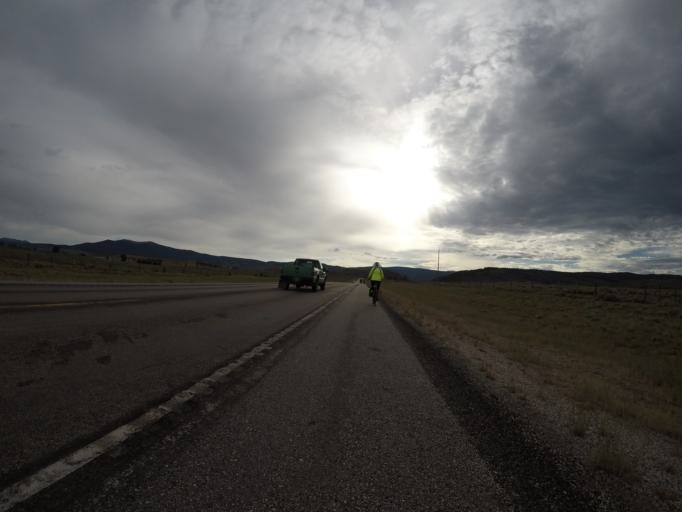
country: US
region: Wyoming
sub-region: Carbon County
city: Saratoga
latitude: 41.3566
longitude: -106.5991
